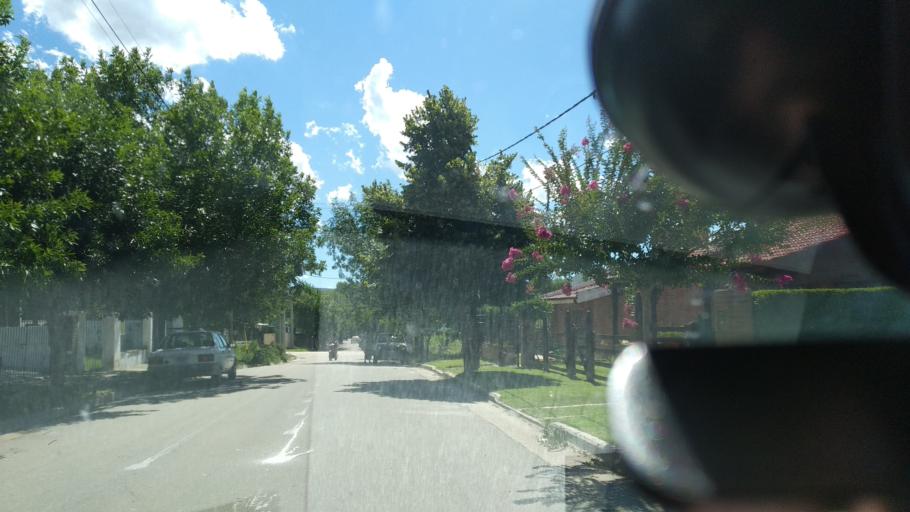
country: AR
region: Cordoba
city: Mina Clavero
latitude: -31.7241
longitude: -65.0102
